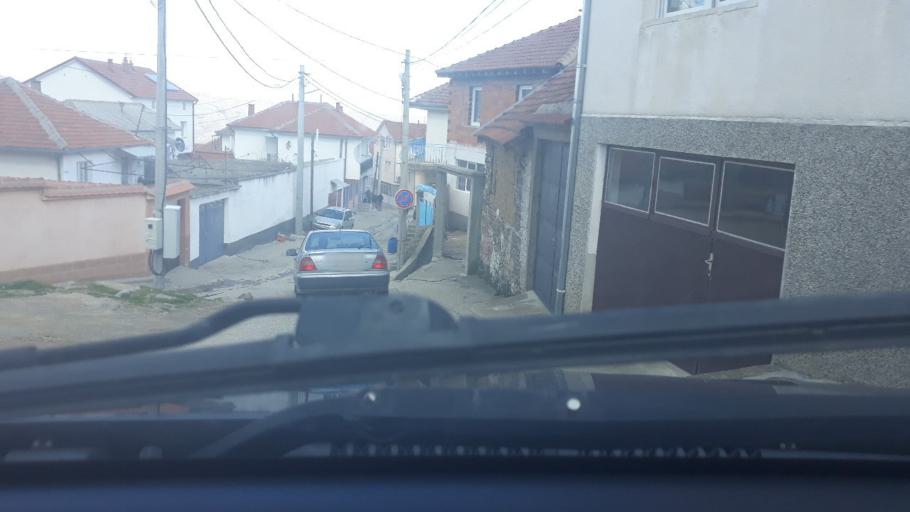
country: MK
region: Caska
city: Caska
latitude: 41.6418
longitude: 21.5893
